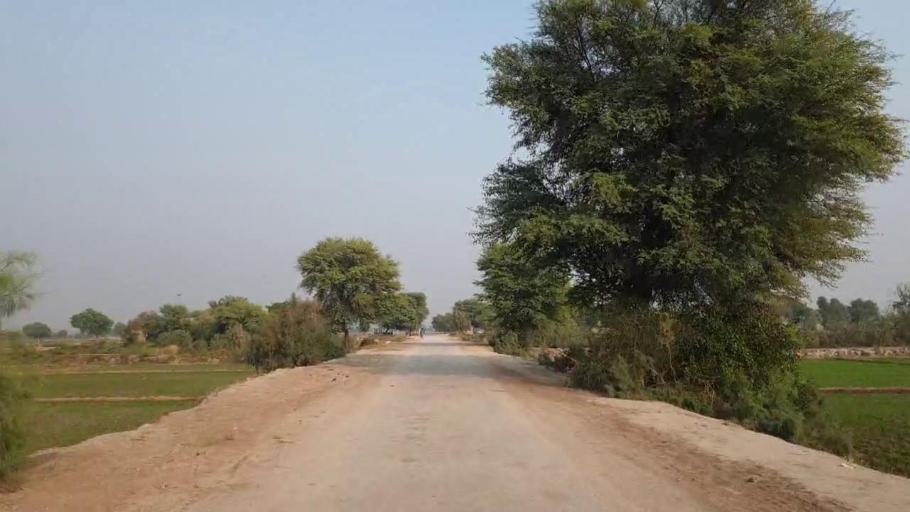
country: PK
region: Sindh
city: Bhan
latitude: 26.4958
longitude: 67.7291
